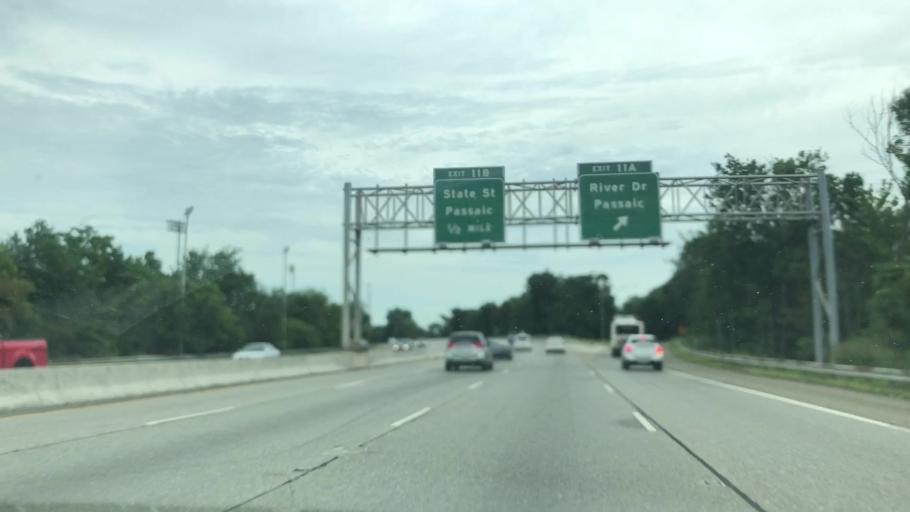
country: US
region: New Jersey
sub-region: Bergen County
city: Wallington
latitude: 40.8479
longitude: -74.1215
